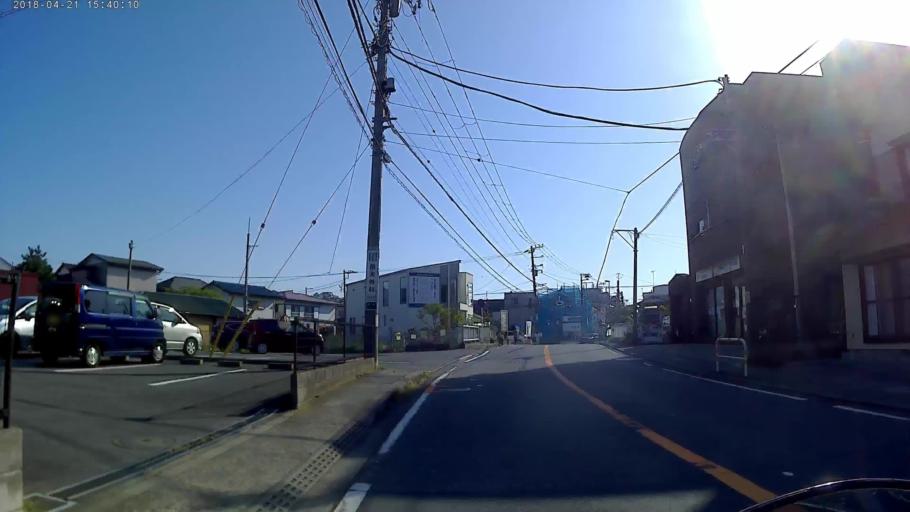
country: JP
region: Kanagawa
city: Fujisawa
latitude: 35.3121
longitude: 139.4990
